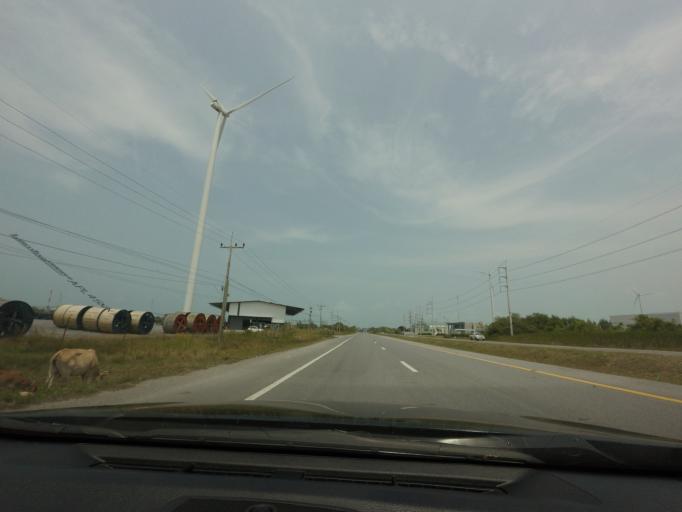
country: TH
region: Nakhon Si Thammarat
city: Hua Sai
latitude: 7.9961
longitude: 100.3164
